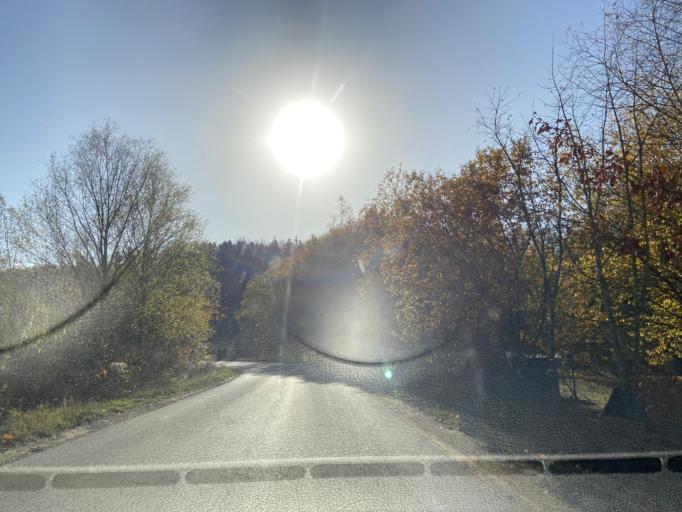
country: DE
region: Baden-Wuerttemberg
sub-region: Tuebingen Region
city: Krauchenwies
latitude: 48.0323
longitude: 9.2737
